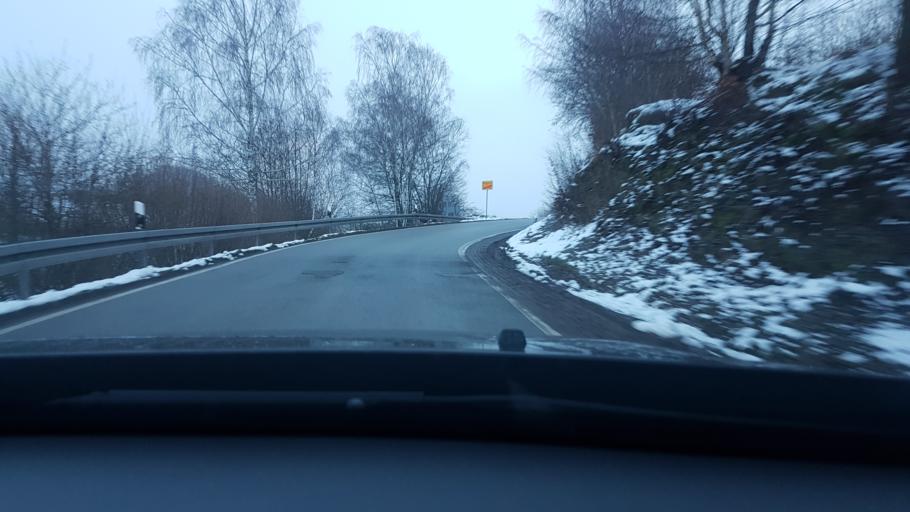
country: DE
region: Hesse
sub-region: Regierungsbezirk Kassel
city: Korbach
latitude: 51.3522
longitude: 8.8984
